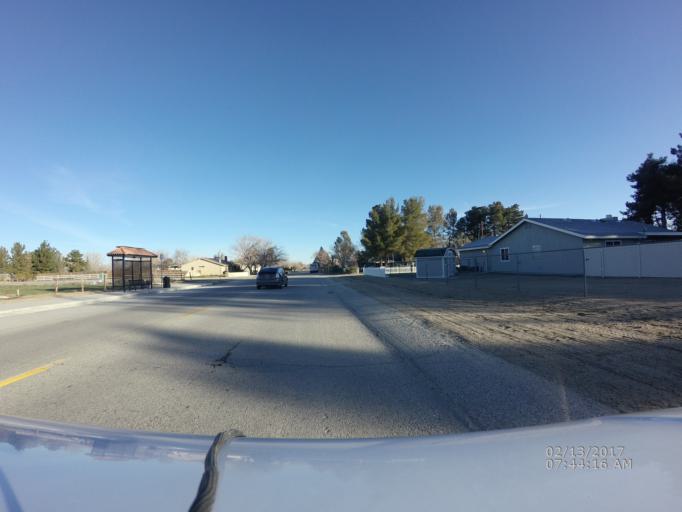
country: US
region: California
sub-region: Los Angeles County
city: Littlerock
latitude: 34.5498
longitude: -117.9581
